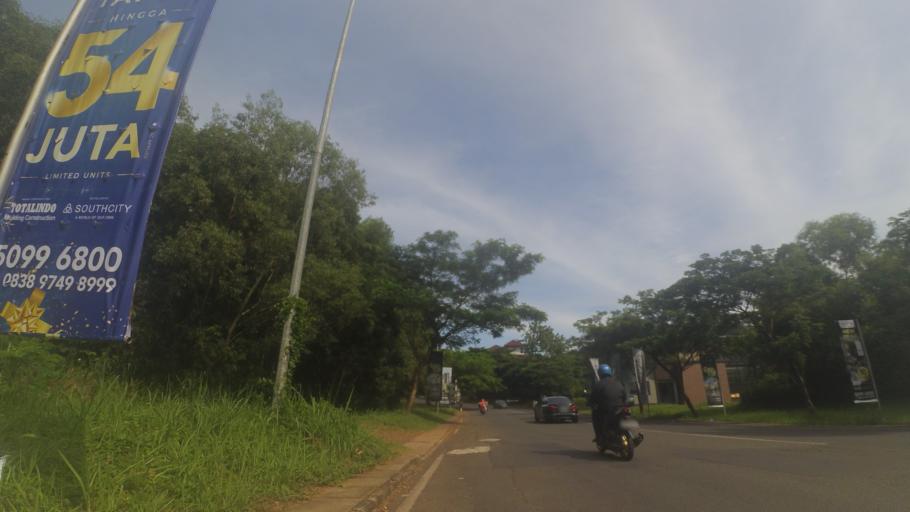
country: ID
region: West Java
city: Pamulang
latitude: -6.3431
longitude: 106.7713
